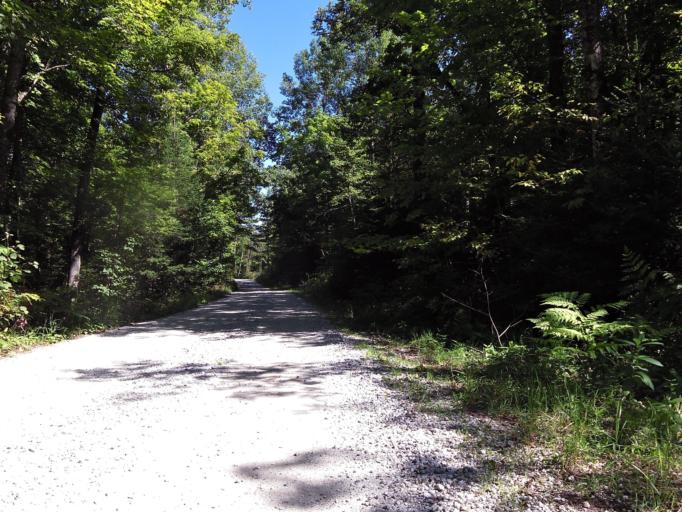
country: CA
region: Ontario
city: Renfrew
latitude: 45.1285
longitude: -76.6905
